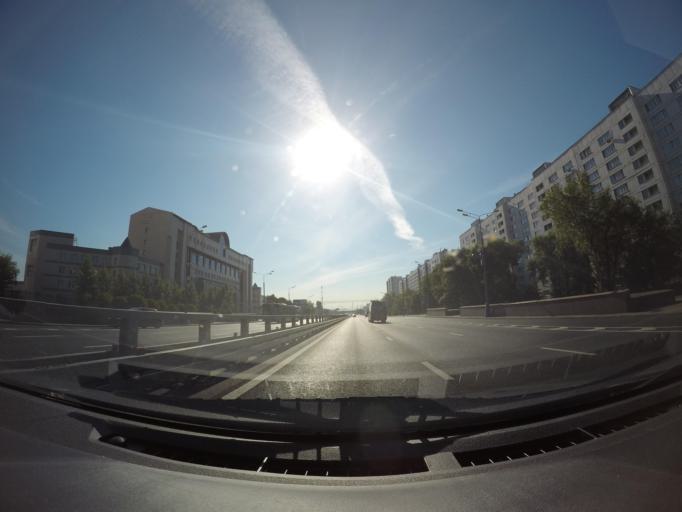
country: RU
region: Moscow
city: Vykhino-Zhulebino
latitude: 55.7140
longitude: 37.8092
